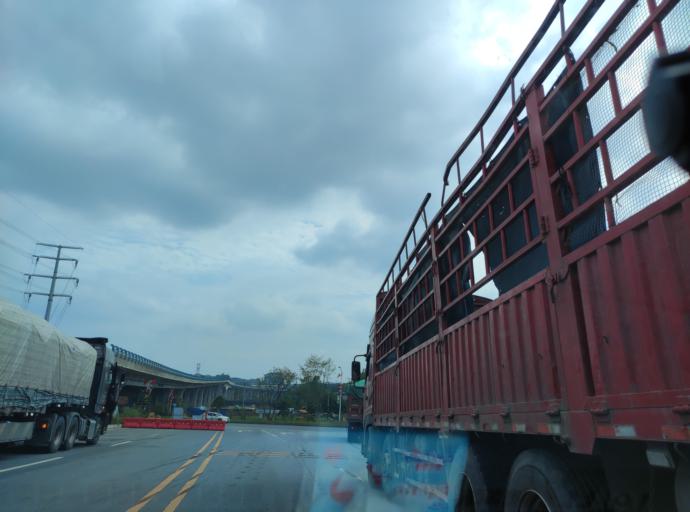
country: CN
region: Jiangxi Sheng
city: Pingxiang
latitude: 27.6625
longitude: 113.9088
